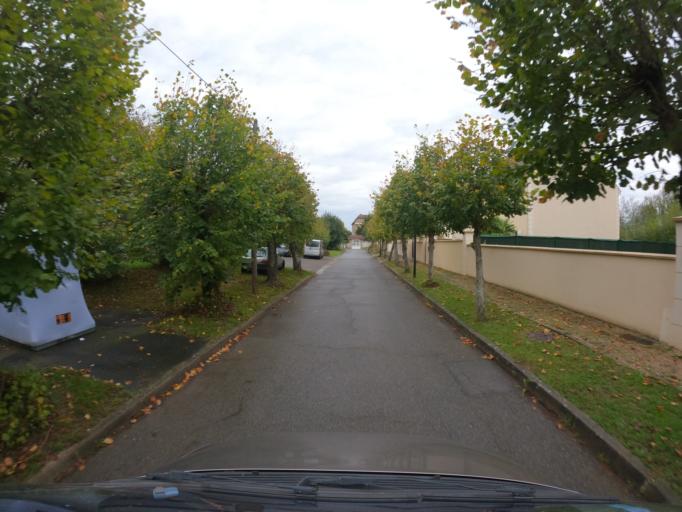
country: FR
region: Ile-de-France
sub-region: Departement de Seine-et-Marne
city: Serris
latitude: 48.8141
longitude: 2.7920
